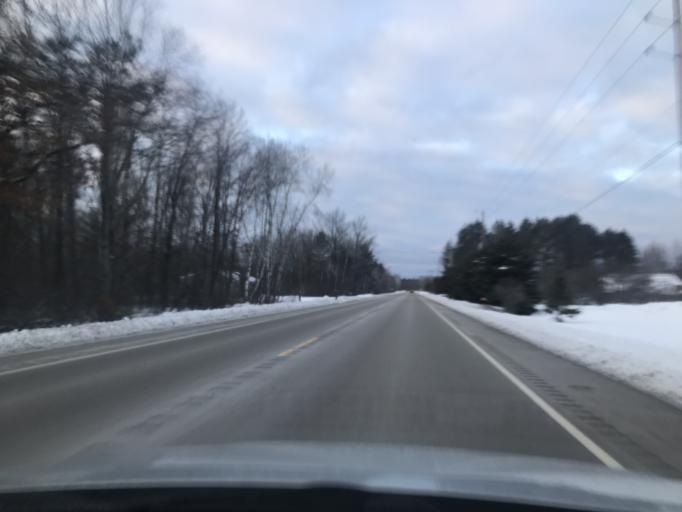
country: US
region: Wisconsin
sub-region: Marinette County
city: Marinette
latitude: 45.1343
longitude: -87.6888
